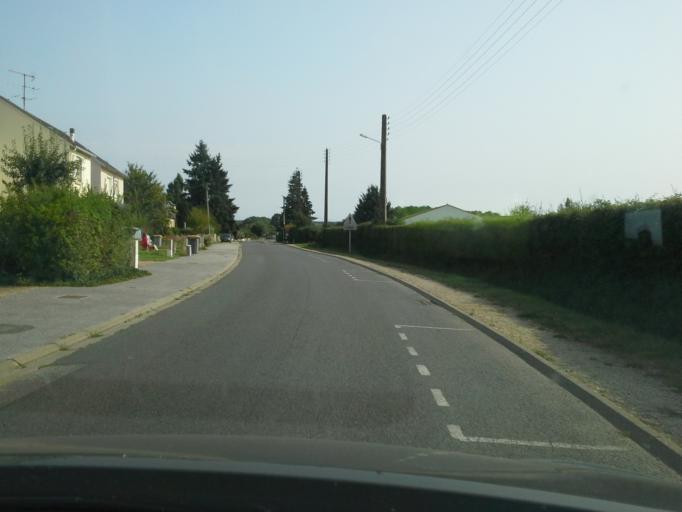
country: FR
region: Centre
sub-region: Departement du Loir-et-Cher
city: La Ville-aux-Clercs
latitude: 47.9157
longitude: 1.0793
